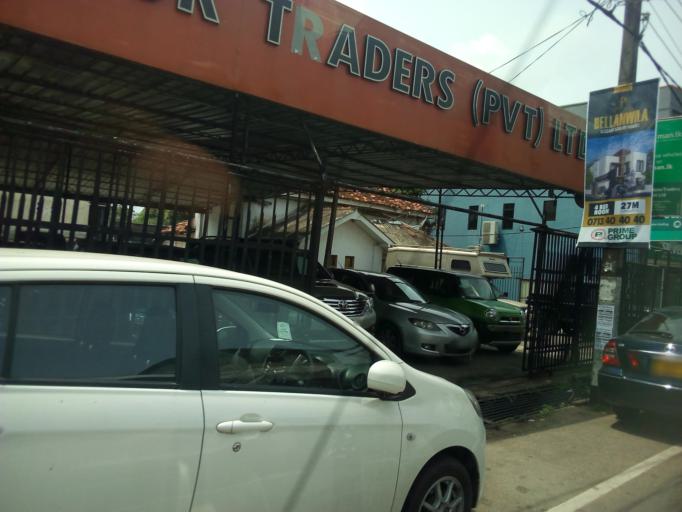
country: LK
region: Western
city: Galkissa
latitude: 6.8385
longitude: 79.8848
